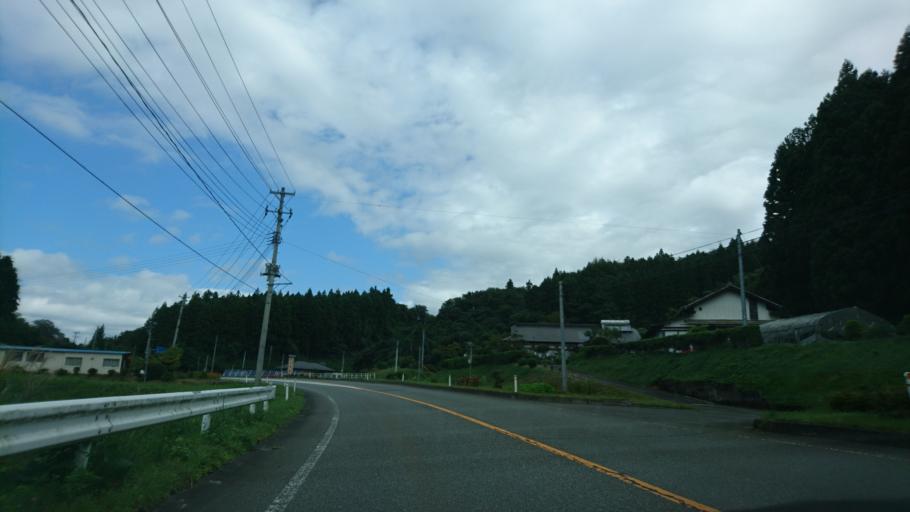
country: JP
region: Miyagi
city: Furukawa
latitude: 38.7716
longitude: 140.8638
